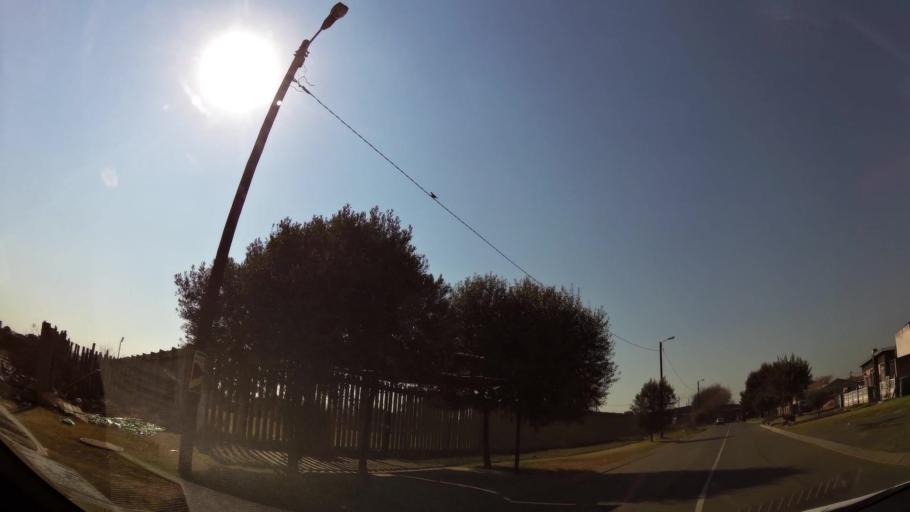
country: ZA
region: Gauteng
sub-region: Ekurhuleni Metropolitan Municipality
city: Boksburg
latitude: -26.2140
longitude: 28.2896
